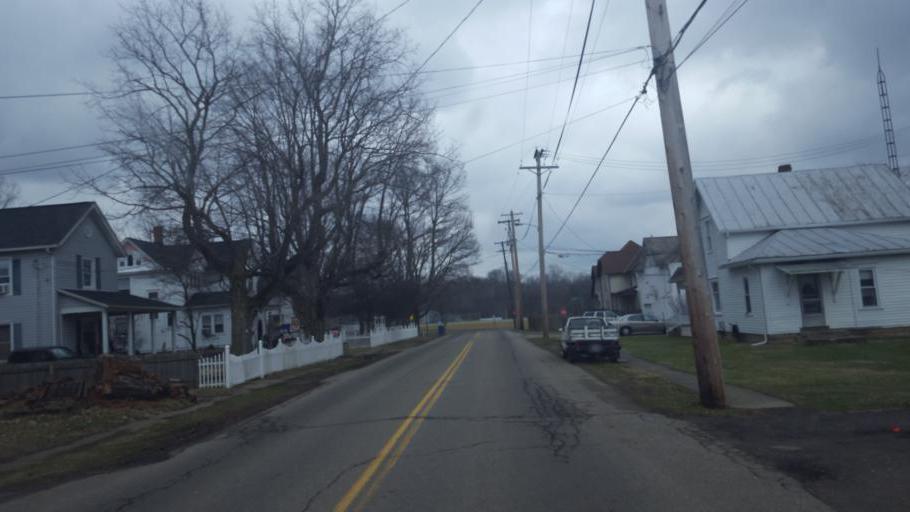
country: US
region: Ohio
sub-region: Knox County
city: Fredericktown
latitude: 40.4875
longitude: -82.5466
